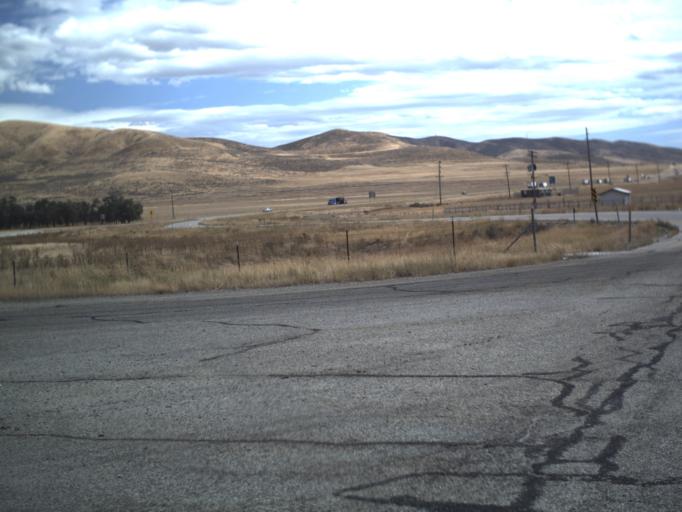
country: US
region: Utah
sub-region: Box Elder County
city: Garland
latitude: 41.8402
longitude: -112.4394
